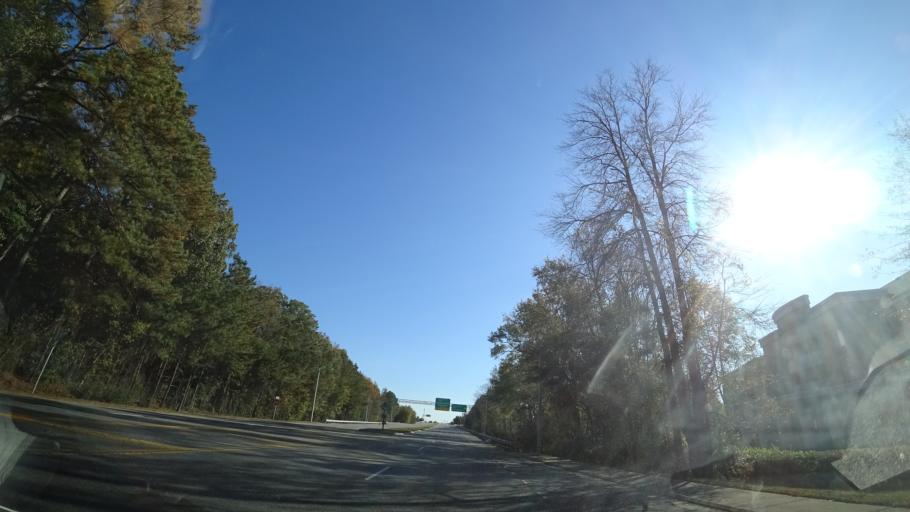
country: US
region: Virginia
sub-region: City of Newport News
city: Newport News
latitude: 36.8927
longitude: -76.4316
